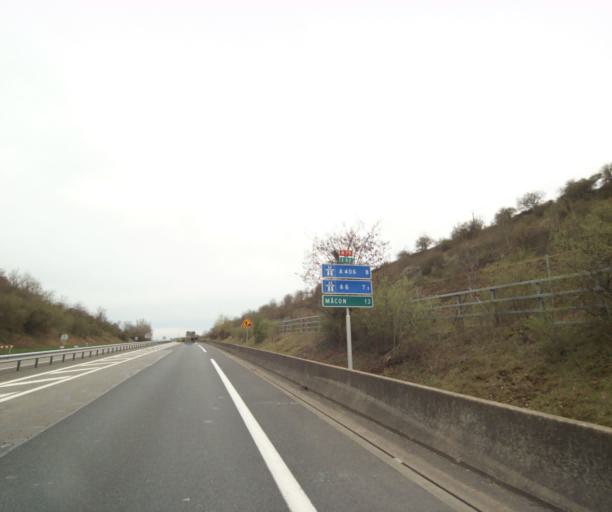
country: FR
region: Bourgogne
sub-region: Departement de Saone-et-Loire
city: Prisse
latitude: 46.3248
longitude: 4.7364
